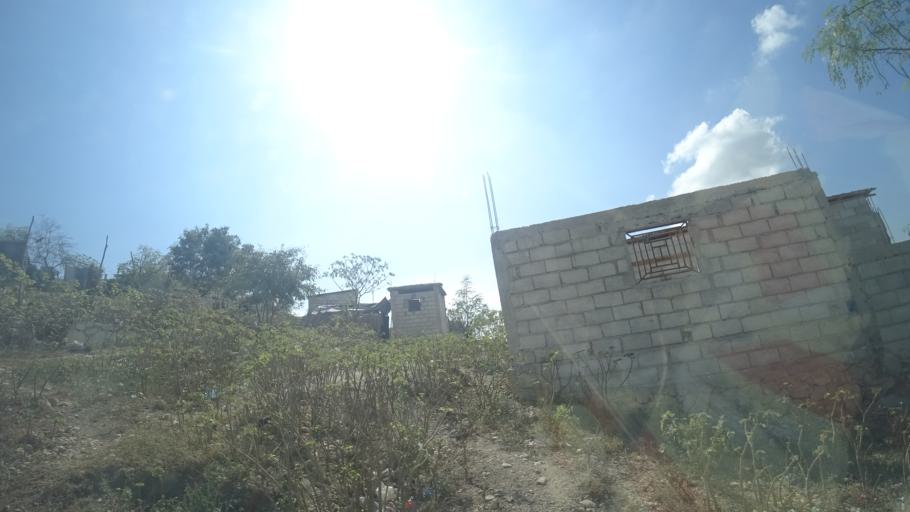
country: HT
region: Ouest
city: Croix des Bouquets
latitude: 18.6591
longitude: -72.2870
